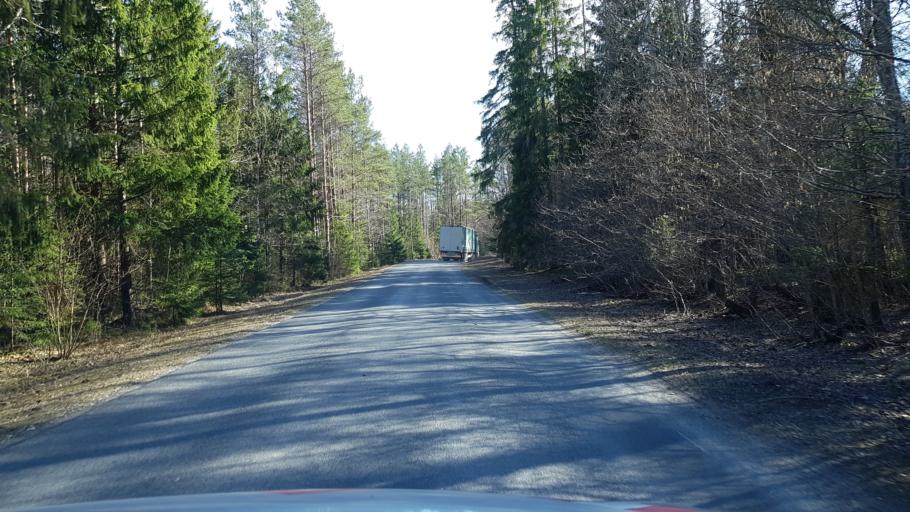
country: EE
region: Harju
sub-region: Nissi vald
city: Riisipere
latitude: 59.0851
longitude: 24.3541
